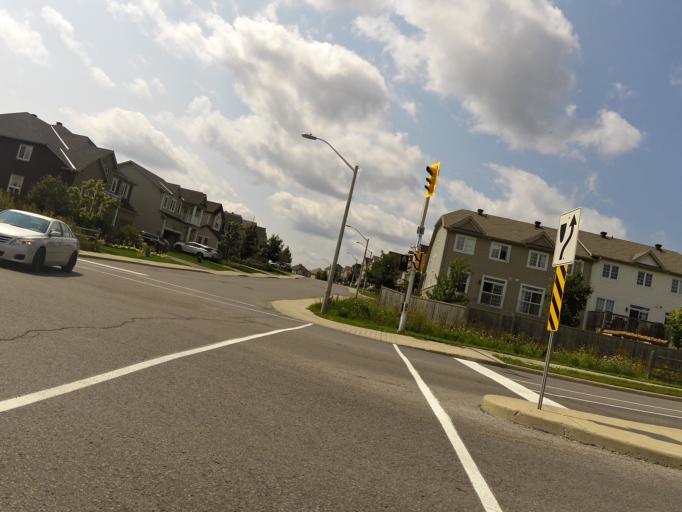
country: CA
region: Ontario
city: Bells Corners
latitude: 45.3151
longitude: -75.9318
